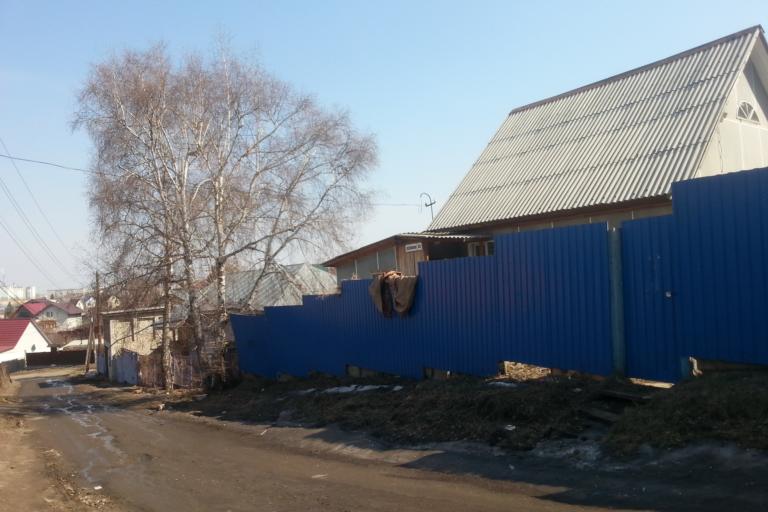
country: RU
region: Altai Krai
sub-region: Gorod Barnaulskiy
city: Barnaul
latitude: 53.3751
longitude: 83.6924
